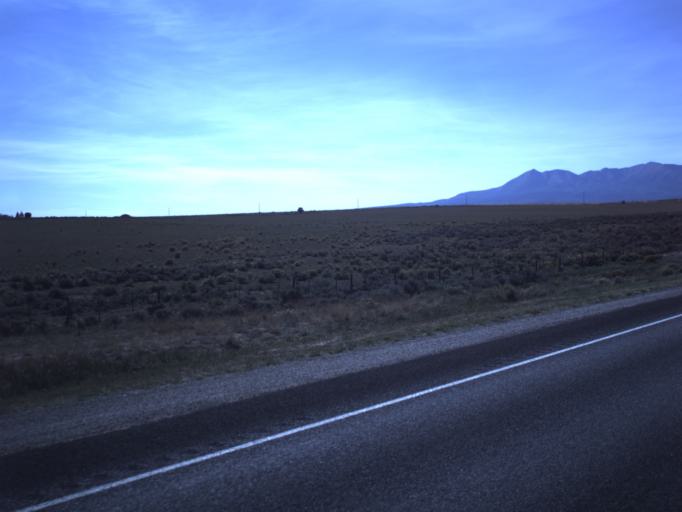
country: US
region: Utah
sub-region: San Juan County
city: Monticello
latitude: 37.8499
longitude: -109.1634
